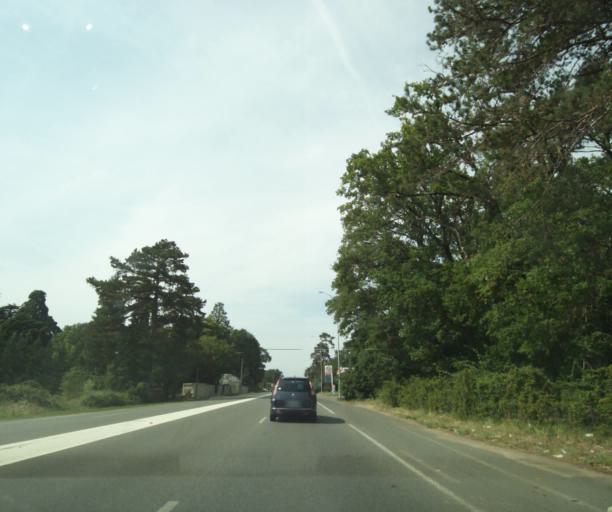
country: FR
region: Centre
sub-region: Departement d'Indre-et-Loire
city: Montbazon
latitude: 47.3081
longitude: 0.7137
